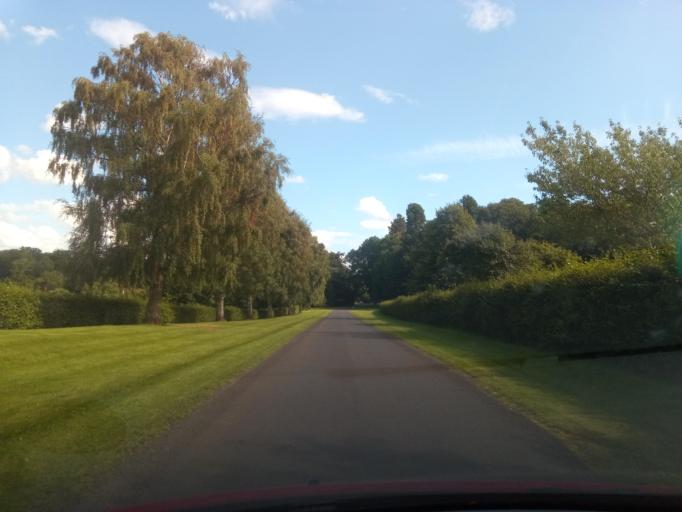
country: GB
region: Scotland
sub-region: The Scottish Borders
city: Coldstream
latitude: 55.6502
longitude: -2.2651
